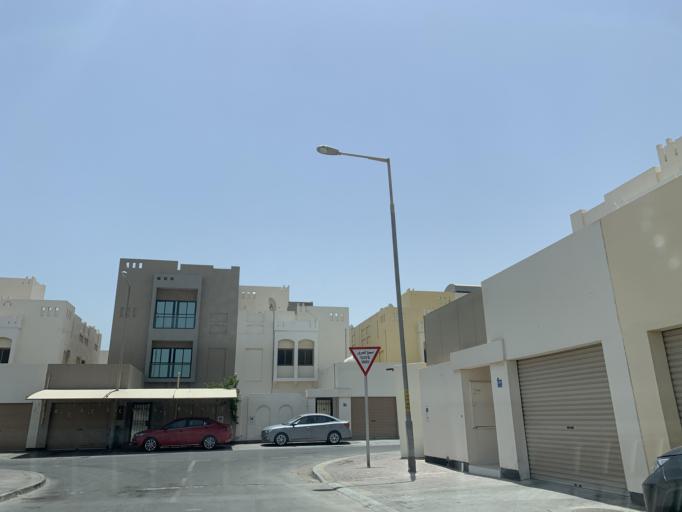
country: BH
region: Northern
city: Sitrah
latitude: 26.1391
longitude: 50.5902
